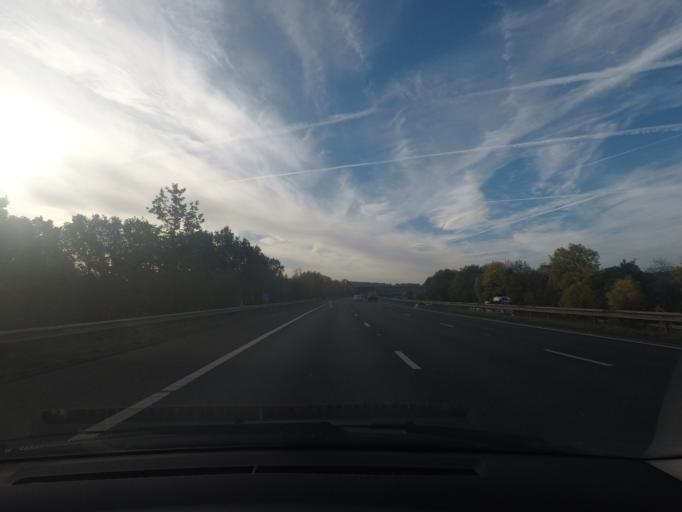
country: GB
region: England
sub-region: City and Borough of Wakefield
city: Crigglestone
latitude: 53.6320
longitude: -1.5399
